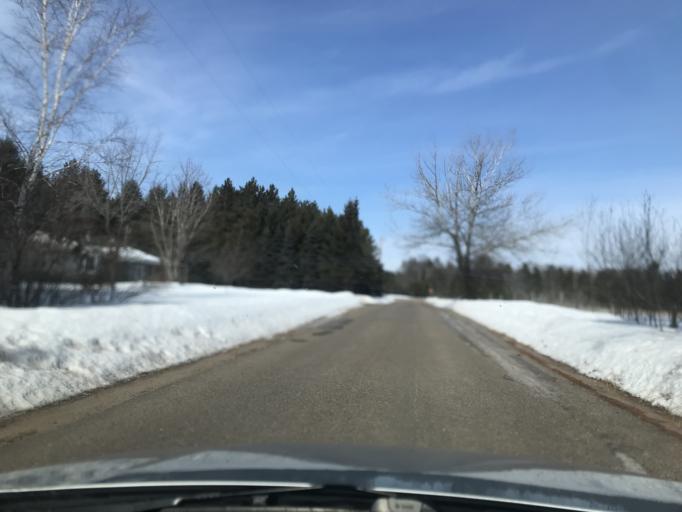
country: US
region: Wisconsin
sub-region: Marinette County
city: Peshtigo
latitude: 45.2262
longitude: -87.9627
